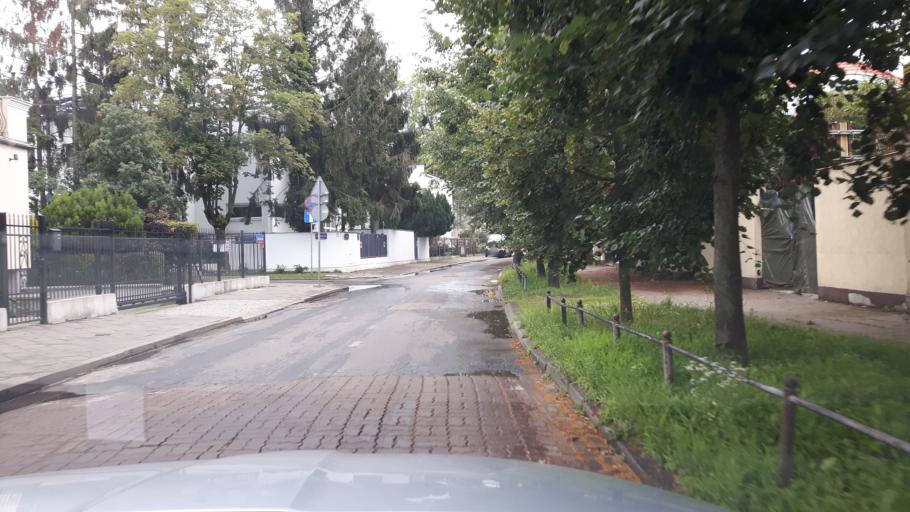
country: PL
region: Masovian Voivodeship
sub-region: Warszawa
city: Praga Polnoc
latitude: 52.2290
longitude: 21.0544
